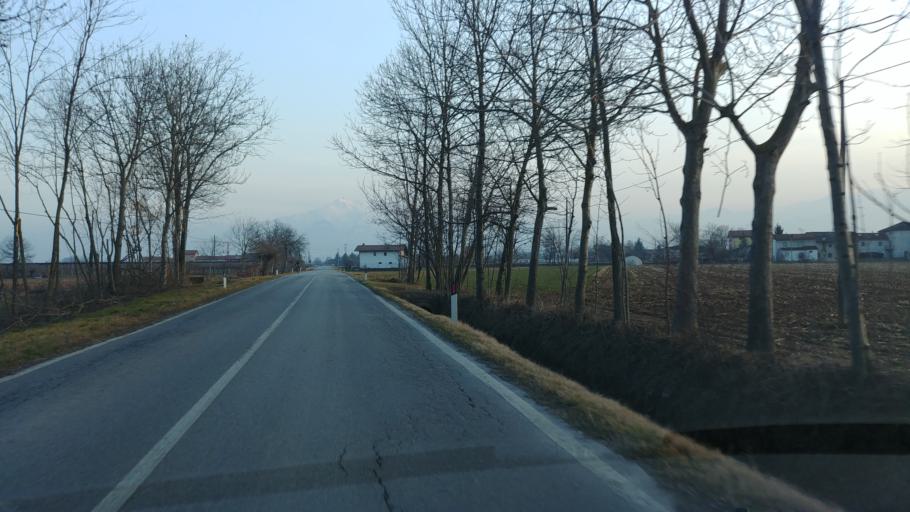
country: IT
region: Piedmont
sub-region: Provincia di Cuneo
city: Roata Rossi
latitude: 44.4196
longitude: 7.5084
